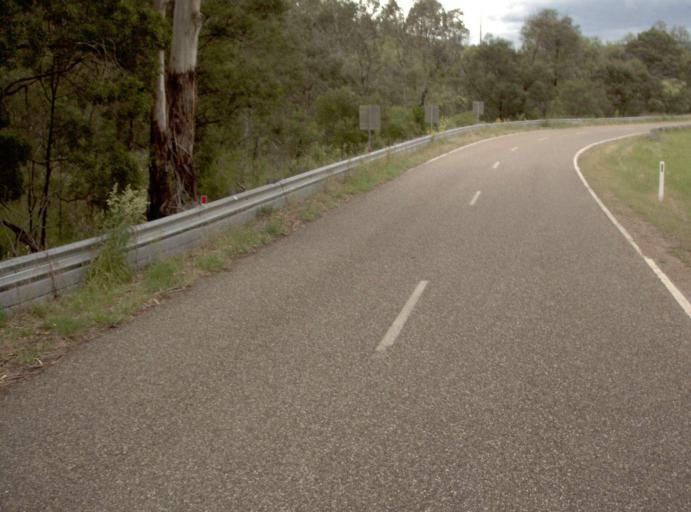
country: AU
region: Victoria
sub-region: East Gippsland
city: Bairnsdale
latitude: -37.5424
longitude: 147.2046
